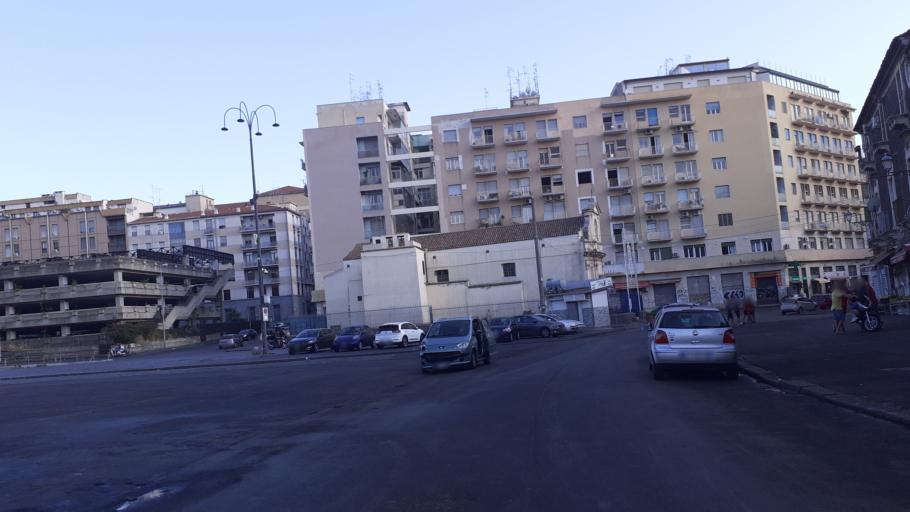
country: IT
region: Sicily
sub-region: Catania
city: Catania
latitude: 37.5095
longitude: 15.0882
